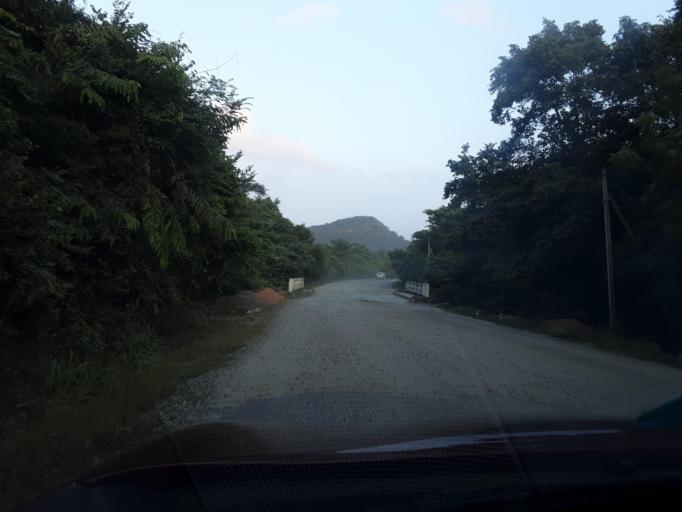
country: LK
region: Central
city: Dambulla
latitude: 7.8108
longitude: 80.7763
